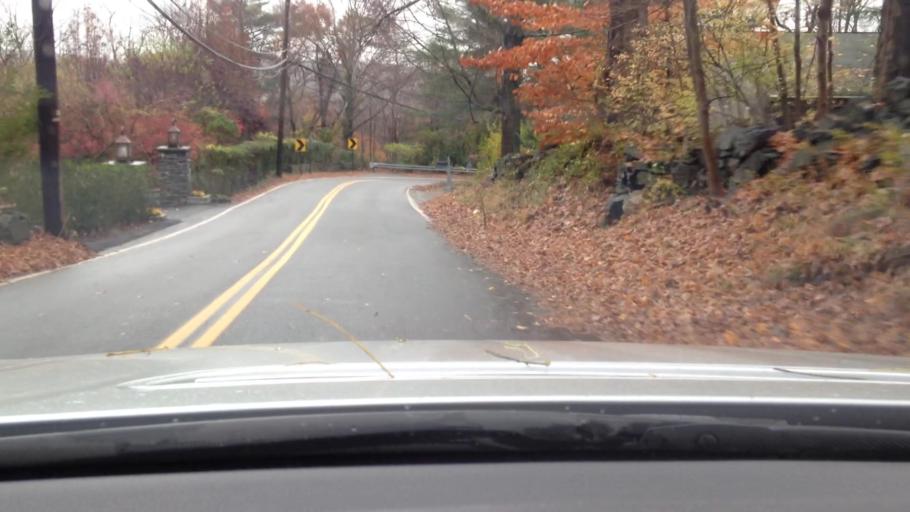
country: US
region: New York
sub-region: Westchester County
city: Croton-on-Hudson
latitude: 41.2219
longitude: -73.8767
